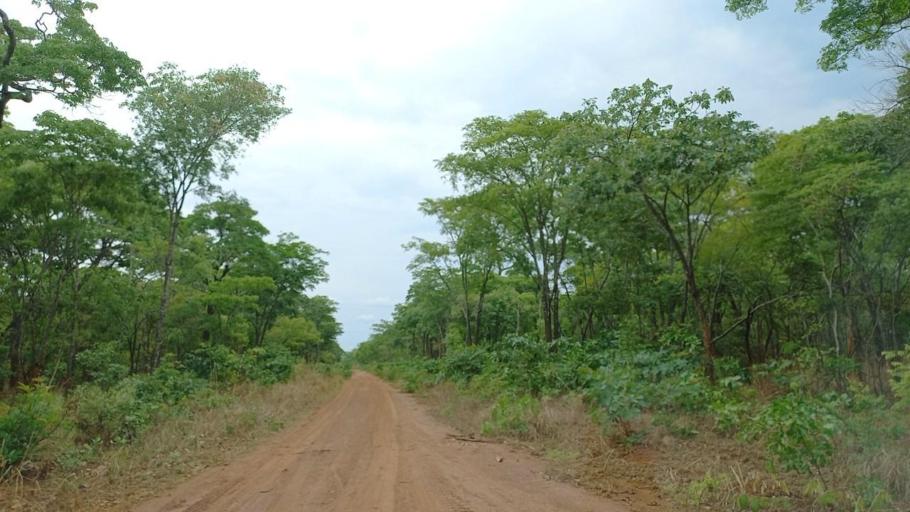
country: ZM
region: North-Western
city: Kalengwa
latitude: -13.5766
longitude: 24.9709
